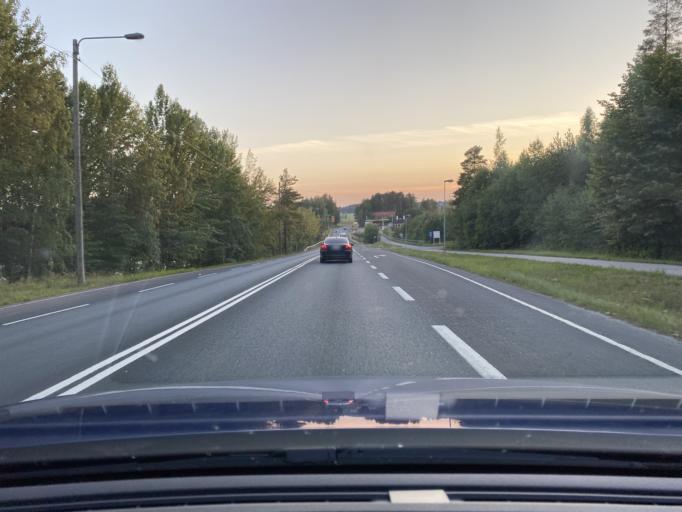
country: FI
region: Pirkanmaa
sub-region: Luoteis-Pirkanmaa
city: Ikaalinen
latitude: 61.7565
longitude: 23.0436
